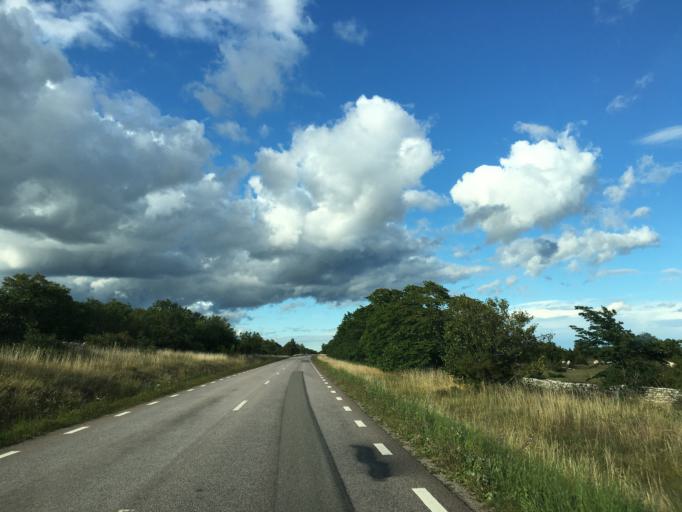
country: SE
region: Kalmar
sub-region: Morbylanga Kommun
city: Moerbylanga
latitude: 56.5589
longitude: 16.4474
